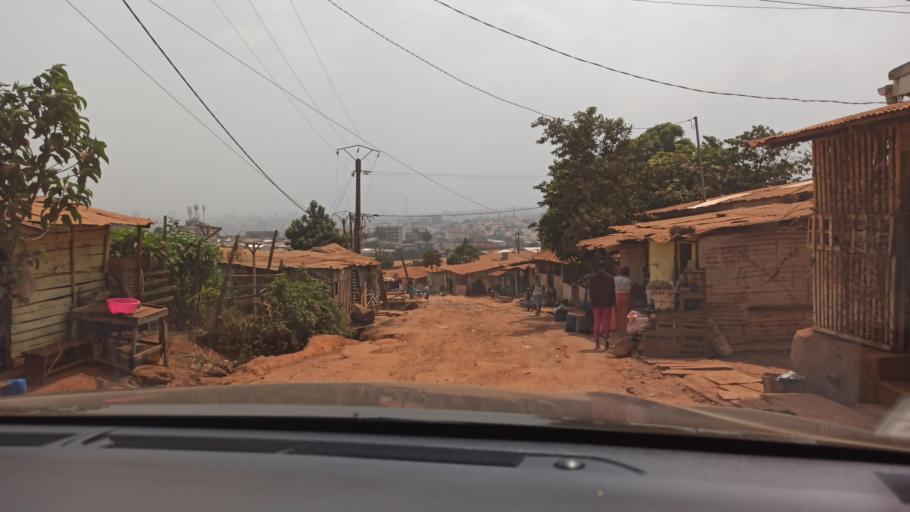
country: CM
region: Centre
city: Yaounde
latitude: 3.8858
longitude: 11.4880
